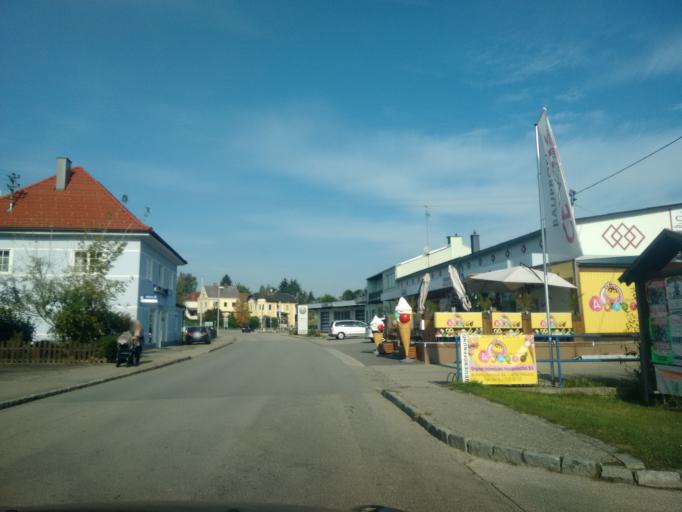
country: AT
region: Upper Austria
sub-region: Politischer Bezirk Ried im Innkreis
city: Ried im Innkreis
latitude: 48.3045
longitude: 13.6318
